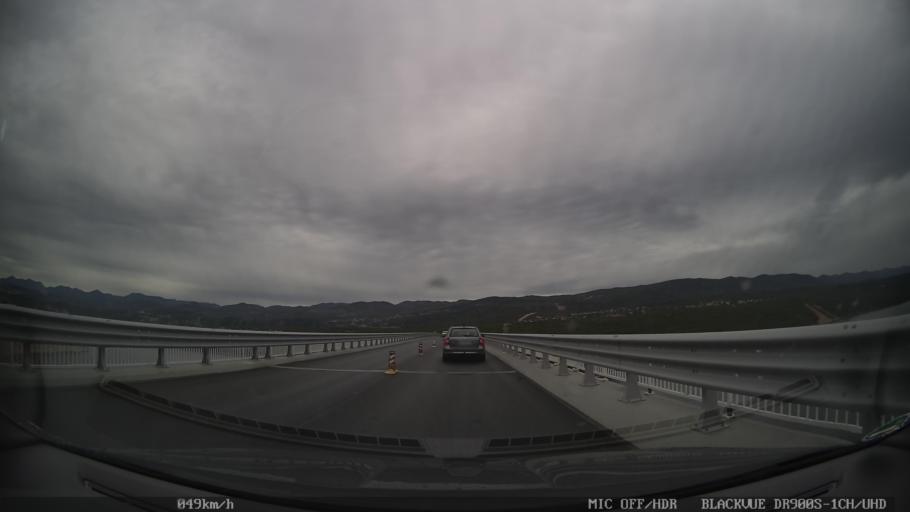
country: HR
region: Primorsko-Goranska
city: Kraljevica
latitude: 45.2471
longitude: 14.5681
